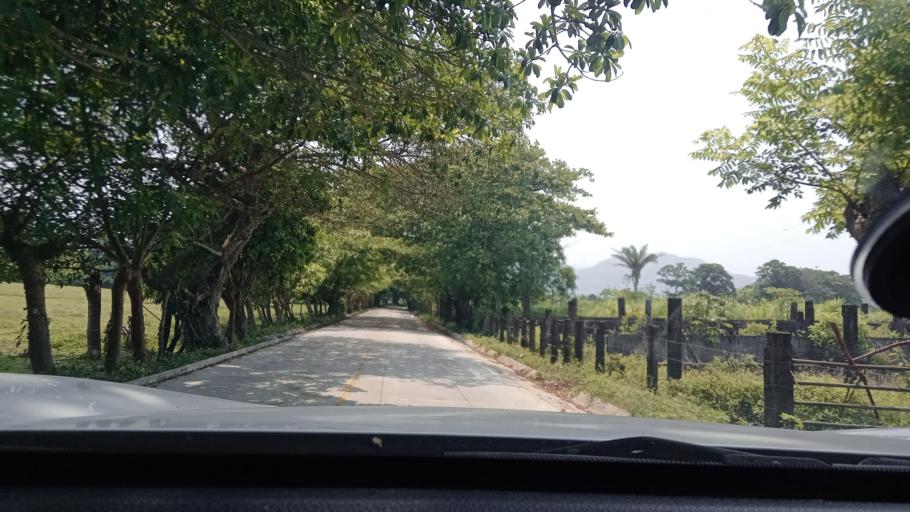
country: MX
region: Veracruz
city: Catemaco
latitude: 18.5606
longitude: -95.0321
